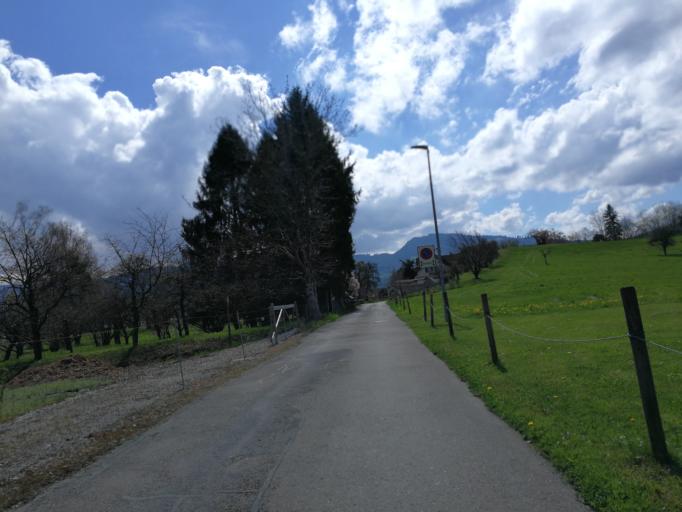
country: CH
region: Zurich
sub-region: Bezirk Meilen
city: Hombrechtikon
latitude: 47.2362
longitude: 8.7780
